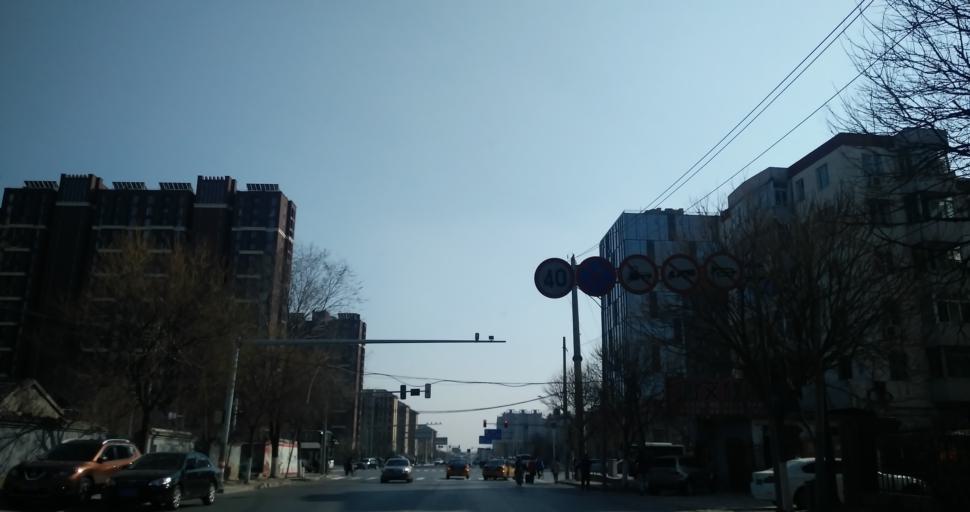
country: CN
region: Beijing
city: Jiugong
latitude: 39.8065
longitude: 116.4499
